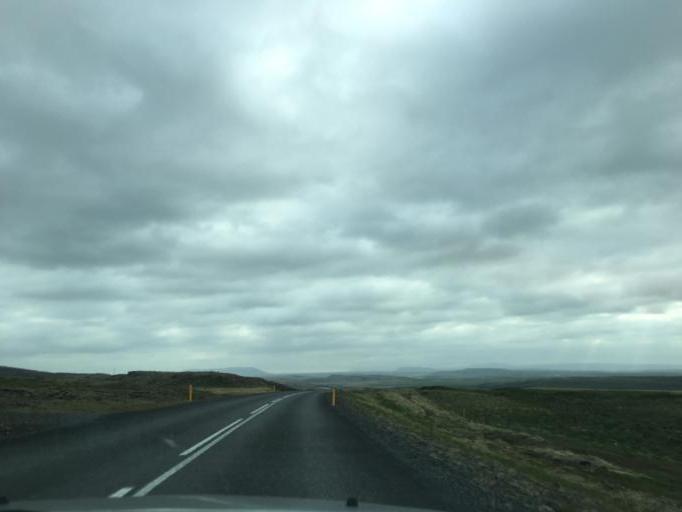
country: IS
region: South
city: Vestmannaeyjar
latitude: 64.2416
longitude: -20.2182
